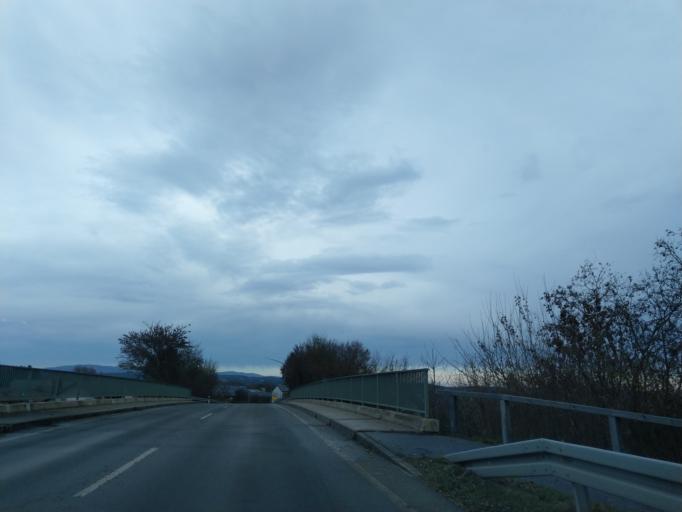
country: DE
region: Bavaria
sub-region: Lower Bavaria
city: Kunzing
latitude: 48.6645
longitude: 13.0694
